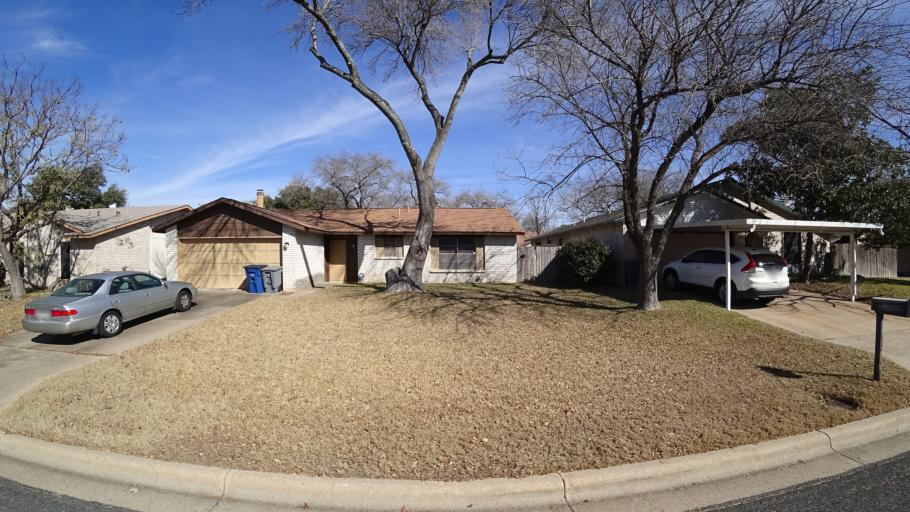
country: US
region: Texas
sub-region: Travis County
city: Wells Branch
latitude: 30.3857
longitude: -97.6970
